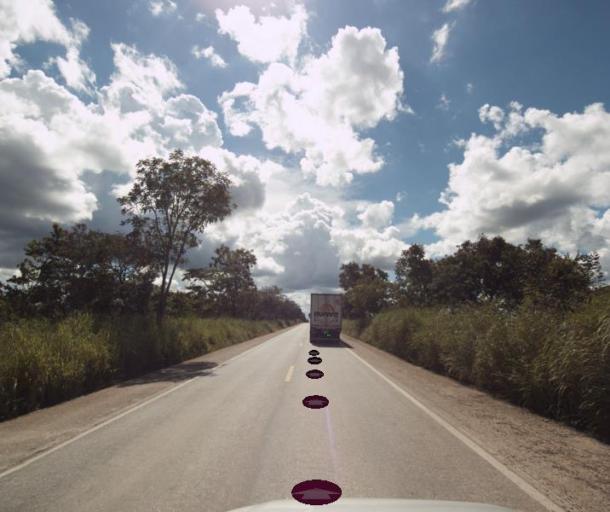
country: BR
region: Goias
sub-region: Porangatu
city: Porangatu
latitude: -13.5628
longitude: -49.0563
